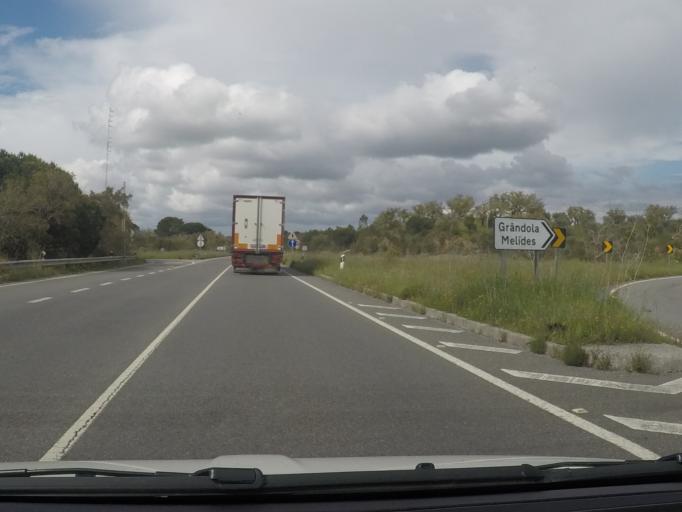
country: PT
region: Setubal
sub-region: Grandola
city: Grandola
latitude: 38.1545
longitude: -8.6495
